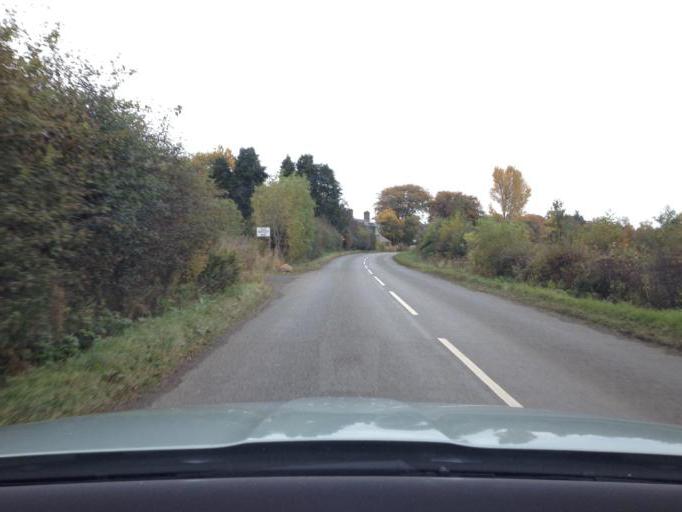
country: GB
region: Scotland
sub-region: Perth and Kinross
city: Stanley
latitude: 56.5113
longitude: -3.4116
